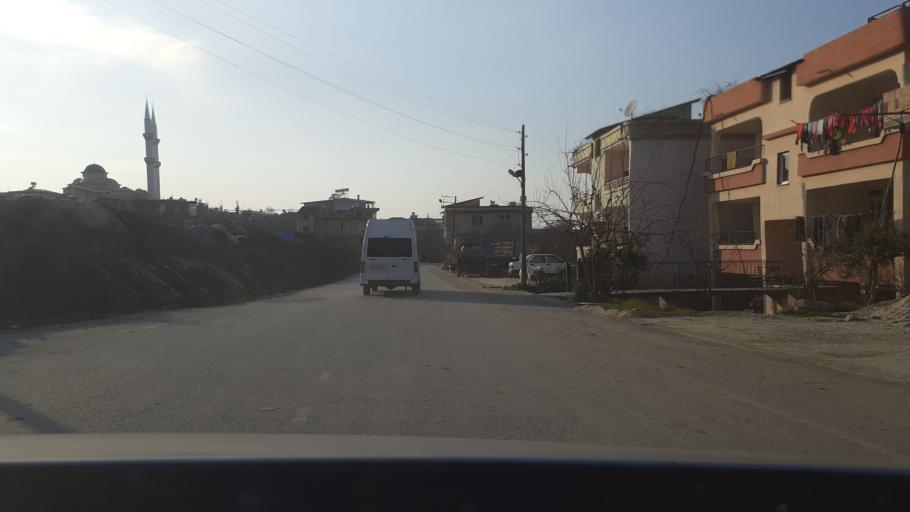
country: TR
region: Hatay
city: Oymakli
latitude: 36.1131
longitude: 36.3008
